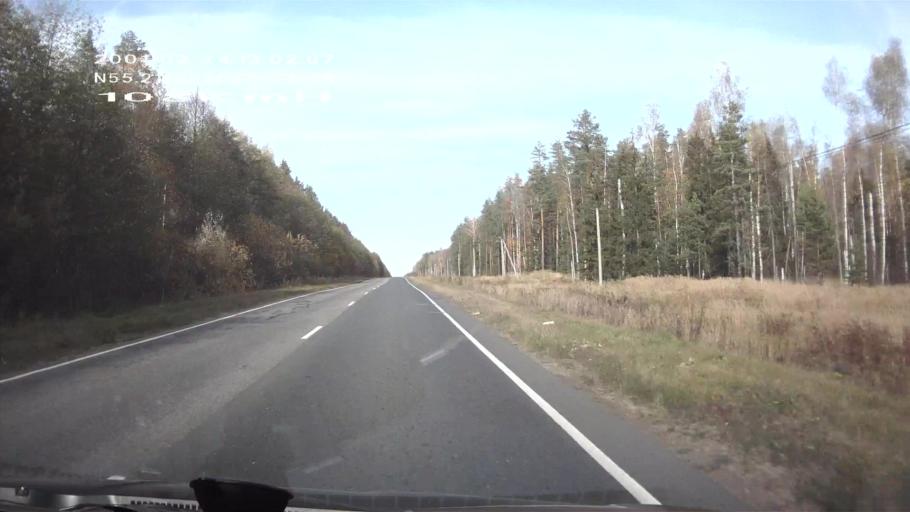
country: RU
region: Chuvashia
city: Buinsk
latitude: 55.2149
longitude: 47.0779
